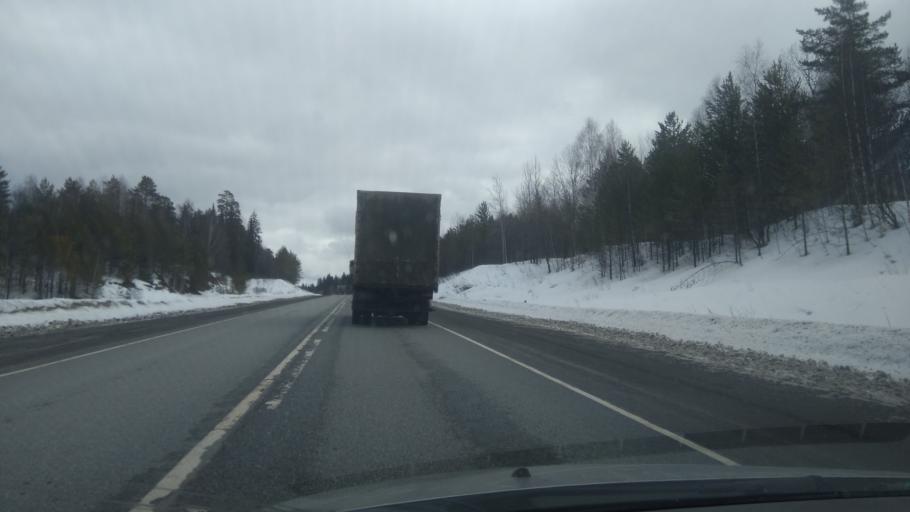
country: RU
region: Sverdlovsk
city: Atig
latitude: 56.8011
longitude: 59.3827
